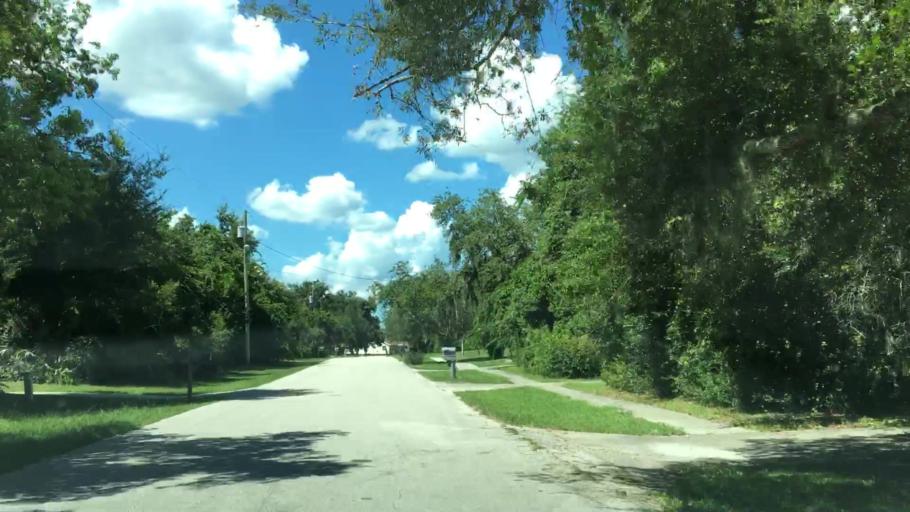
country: US
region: Florida
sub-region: Volusia County
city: Deltona
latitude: 28.8775
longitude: -81.2226
